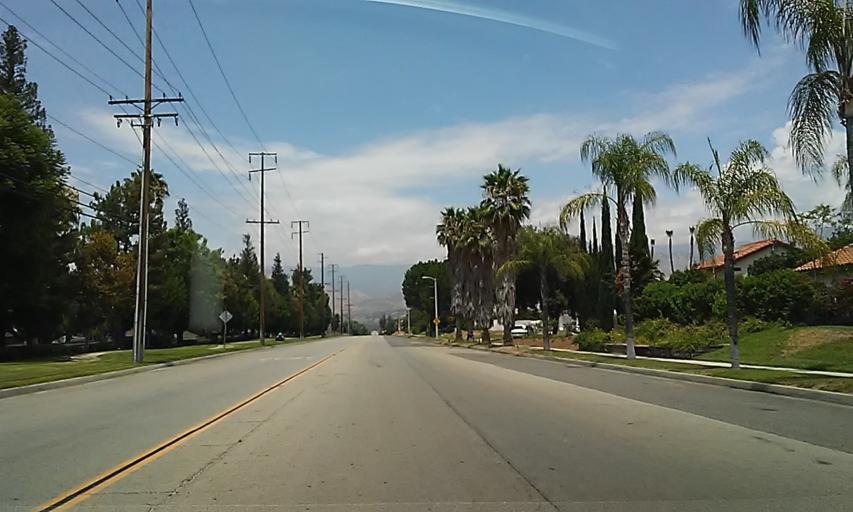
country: US
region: California
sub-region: San Bernardino County
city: Redlands
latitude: 34.0817
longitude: -117.1824
